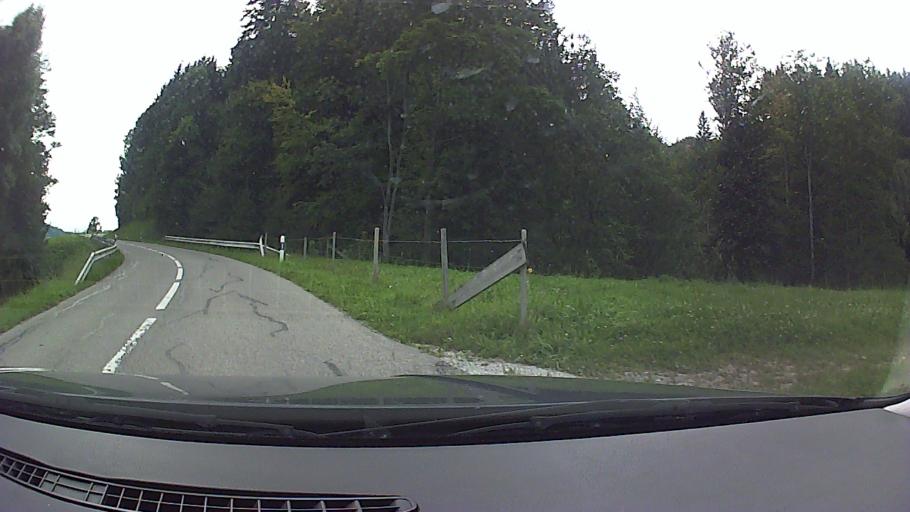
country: CH
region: Fribourg
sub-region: Veveyse District
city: Chatel-Saint-Denis
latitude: 46.5934
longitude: 6.9077
